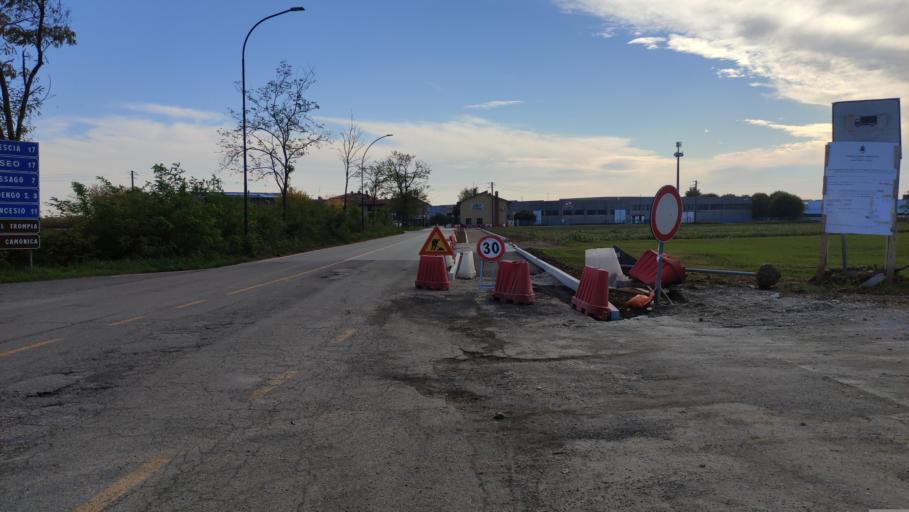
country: IT
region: Lombardy
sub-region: Provincia di Brescia
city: Paderno Franciacorta
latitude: 45.5819
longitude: 10.0833
